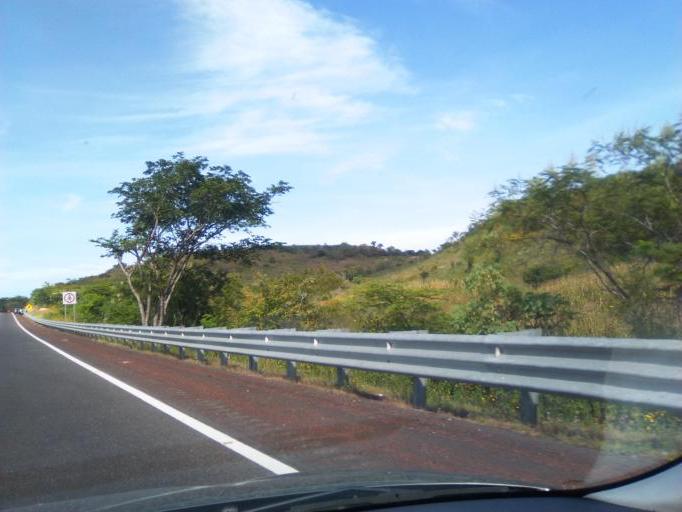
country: MX
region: Guerrero
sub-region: Huitzuco de los Figueroa
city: San Francisco Ozomatlan
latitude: 18.0605
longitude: -99.2476
